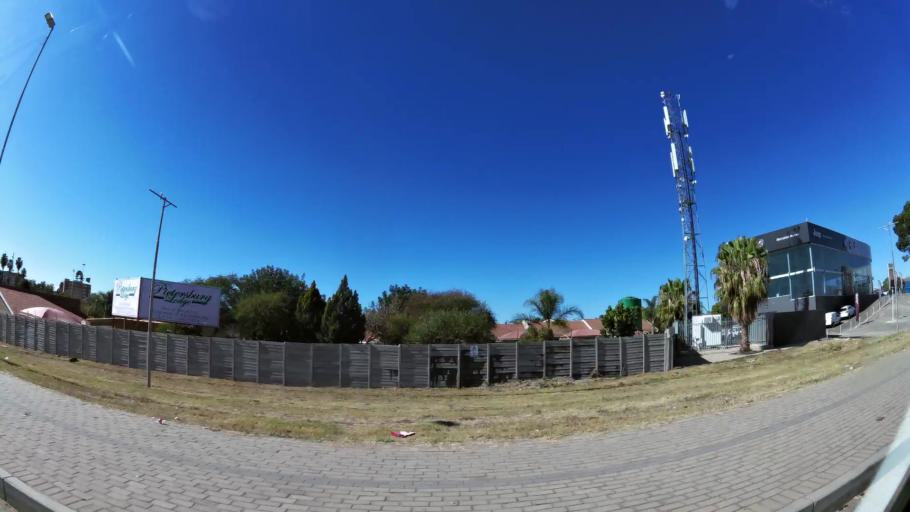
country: ZA
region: Limpopo
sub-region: Capricorn District Municipality
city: Polokwane
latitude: -23.9150
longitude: 29.4443
